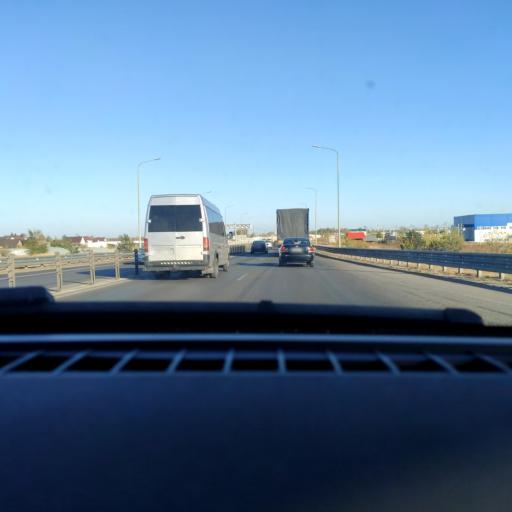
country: RU
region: Voronezj
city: Somovo
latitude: 51.6776
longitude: 39.3065
